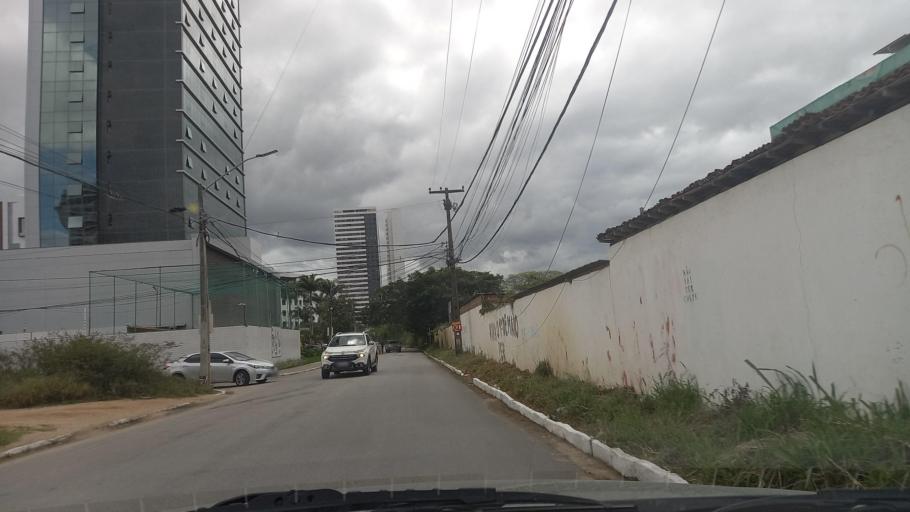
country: BR
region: Pernambuco
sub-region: Caruaru
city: Caruaru
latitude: -8.2619
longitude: -35.9658
